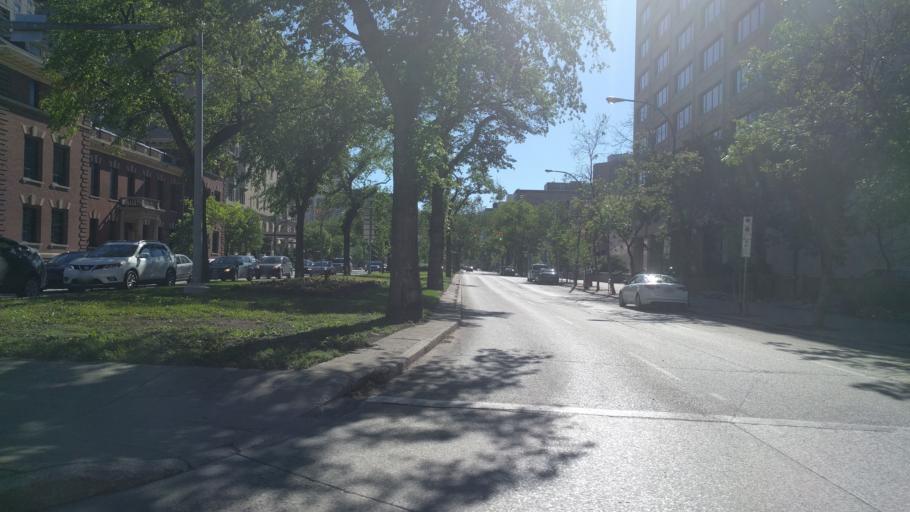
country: CA
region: Manitoba
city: Winnipeg
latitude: 49.8892
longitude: -97.1354
